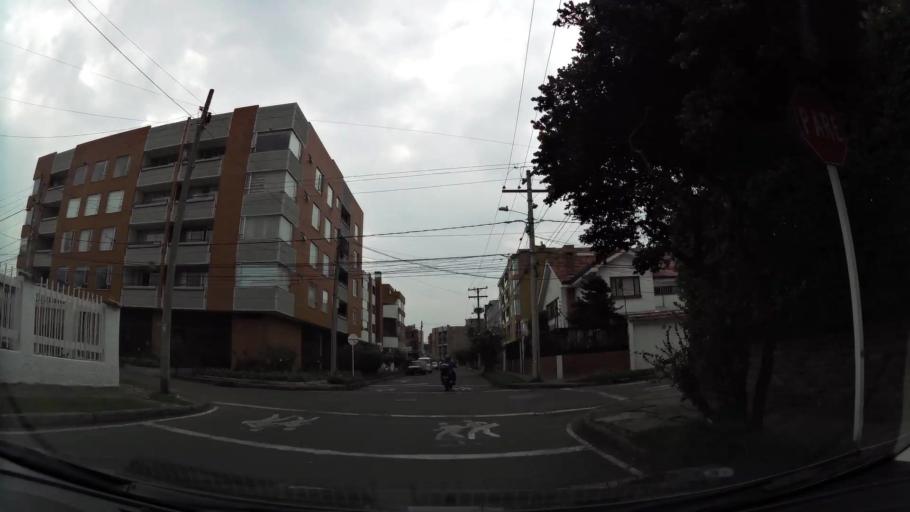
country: CO
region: Bogota D.C.
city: Barrio San Luis
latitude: 4.7181
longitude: -74.0445
